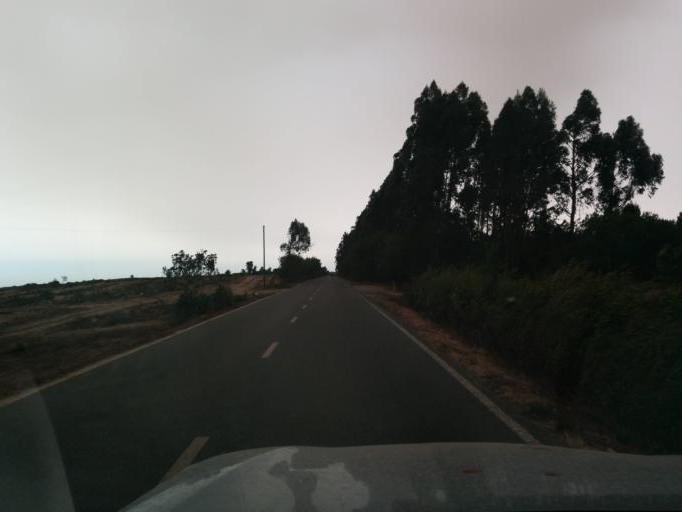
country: PT
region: Beja
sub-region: Odemira
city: Sao Teotonio
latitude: 37.5411
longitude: -8.7499
